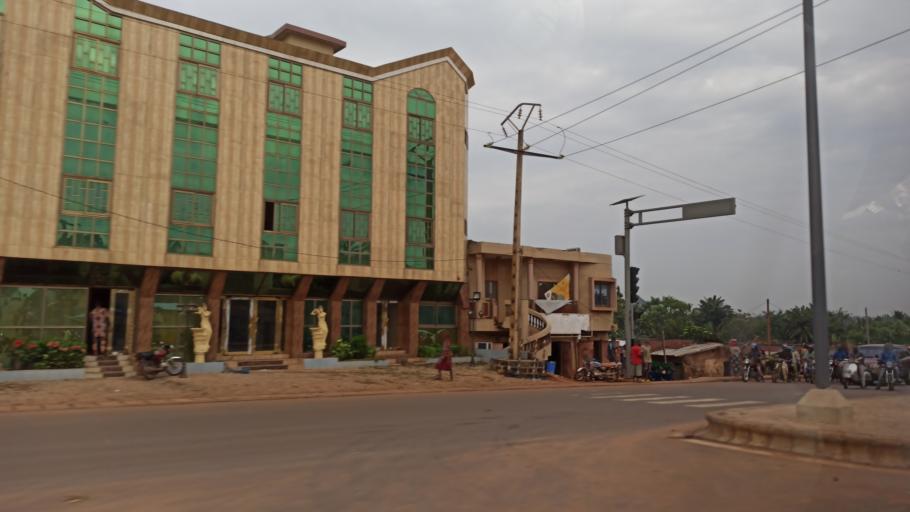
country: BJ
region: Queme
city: Porto-Novo
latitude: 6.5255
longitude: 2.6014
